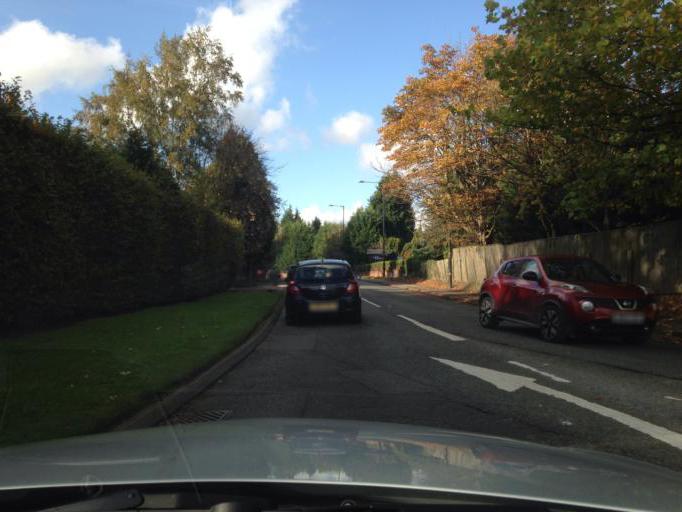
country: GB
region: England
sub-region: Manchester
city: Ringway
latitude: 53.3636
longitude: -2.2984
